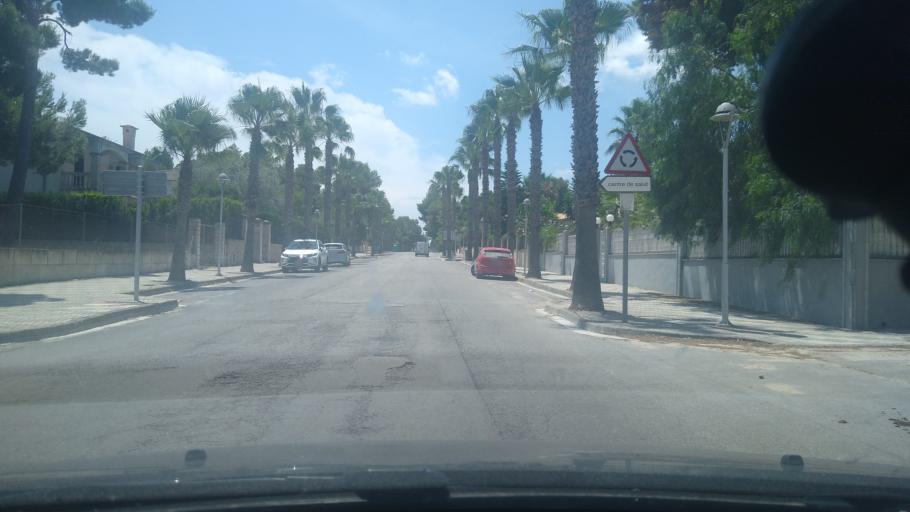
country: ES
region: Balearic Islands
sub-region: Illes Balears
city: Santa Margalida
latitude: 39.7588
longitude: 3.1589
